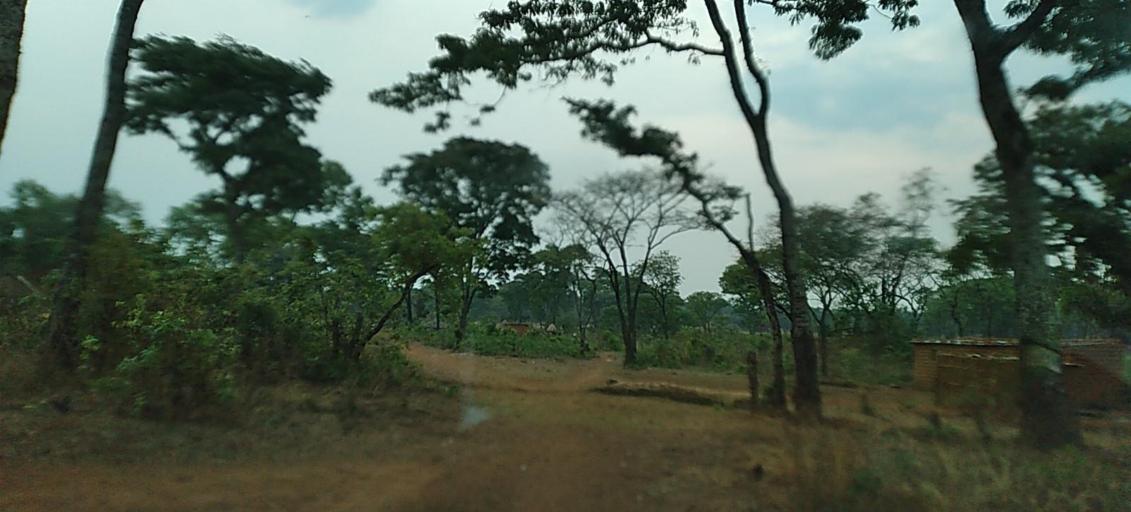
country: ZM
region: North-Western
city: Solwezi
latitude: -12.0441
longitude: 26.0054
